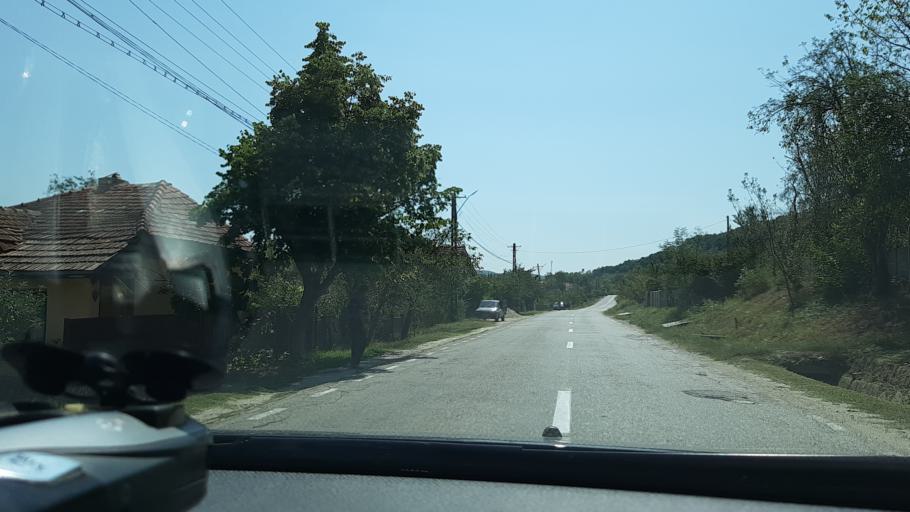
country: RO
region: Gorj
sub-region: Comuna Hurezani
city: Hurezani
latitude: 44.8305
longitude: 23.6425
